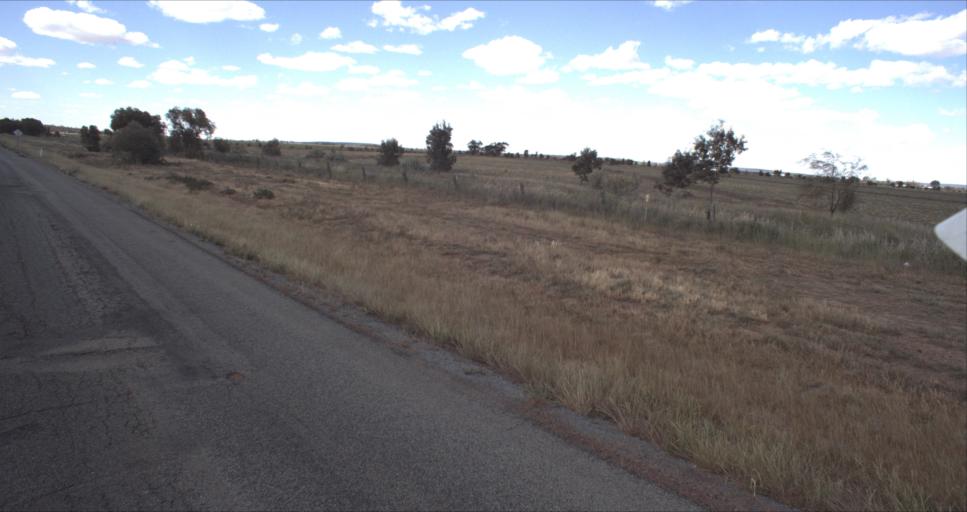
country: AU
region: New South Wales
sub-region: Leeton
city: Leeton
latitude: -34.4439
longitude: 146.2559
